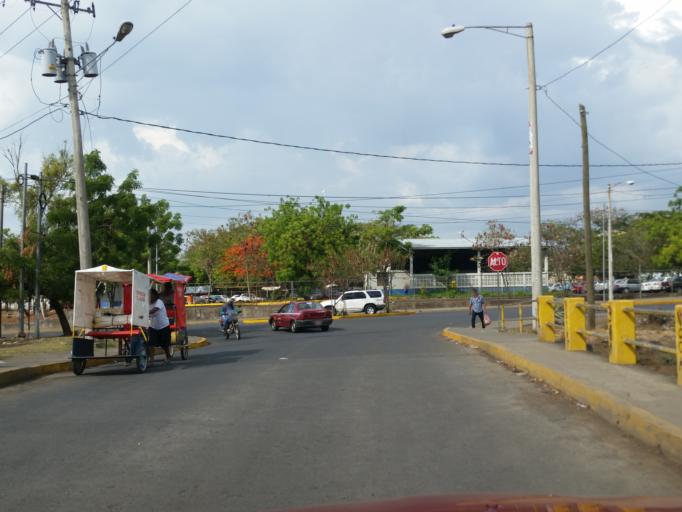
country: NI
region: Managua
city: Managua
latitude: 12.1240
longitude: -86.2462
